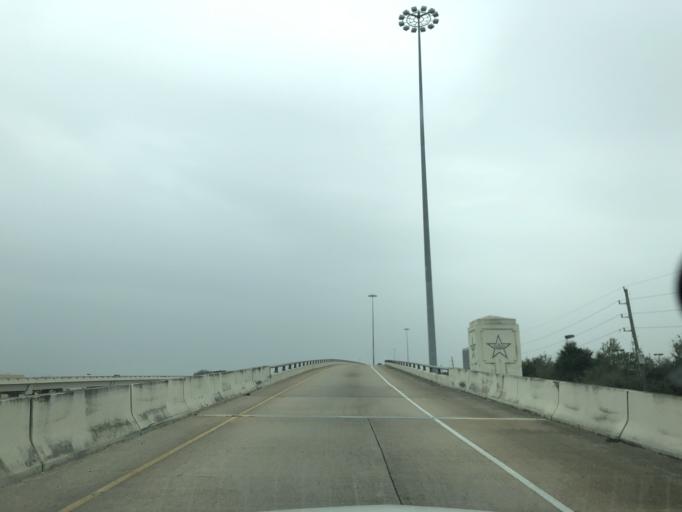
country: US
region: Texas
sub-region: Fort Bend County
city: Meadows Place
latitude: 29.6255
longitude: -95.5966
